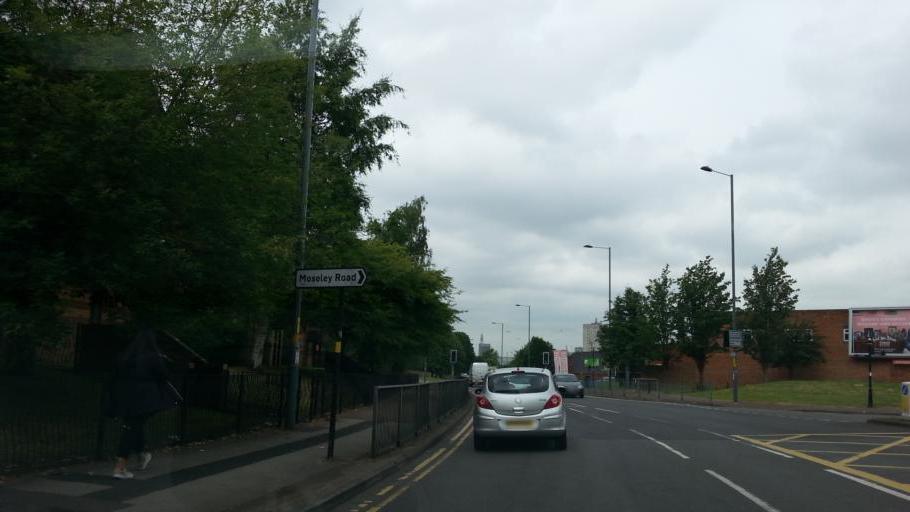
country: GB
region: England
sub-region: City and Borough of Birmingham
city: Birmingham
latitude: 52.4583
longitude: -1.8855
